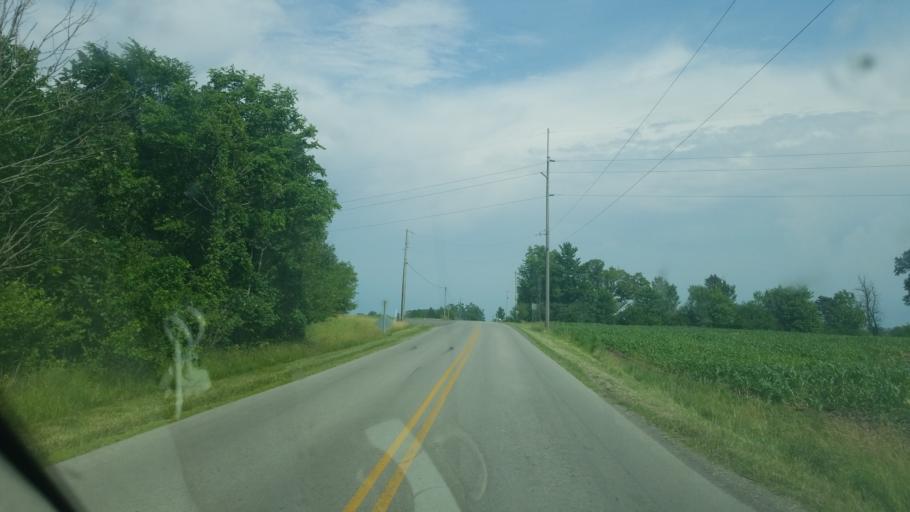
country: US
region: Ohio
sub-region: Champaign County
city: North Lewisburg
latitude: 40.2955
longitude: -83.6416
